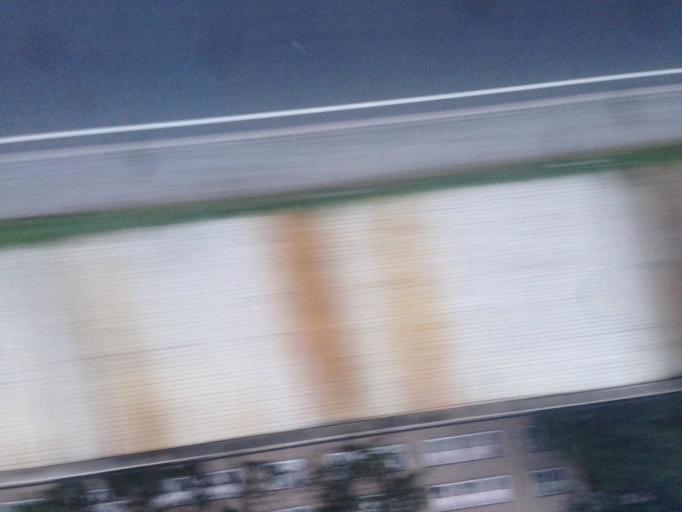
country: US
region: New York
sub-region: Kings County
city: Brooklyn
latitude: 40.6466
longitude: -73.9746
